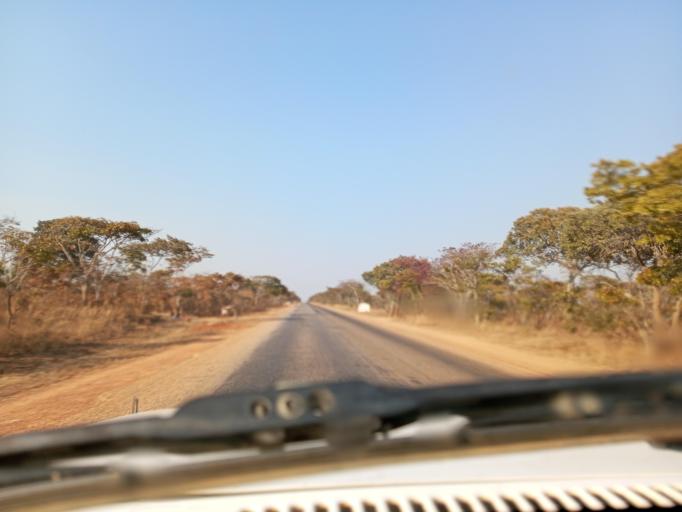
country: ZM
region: Northern
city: Mpika
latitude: -12.3840
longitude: 31.0964
